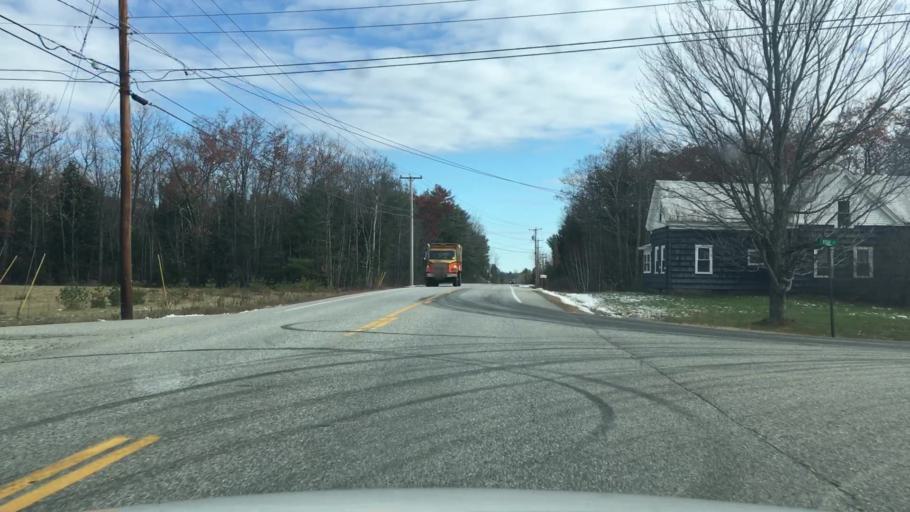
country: US
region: Maine
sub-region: Androscoggin County
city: Leeds
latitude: 44.3439
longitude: -70.1706
